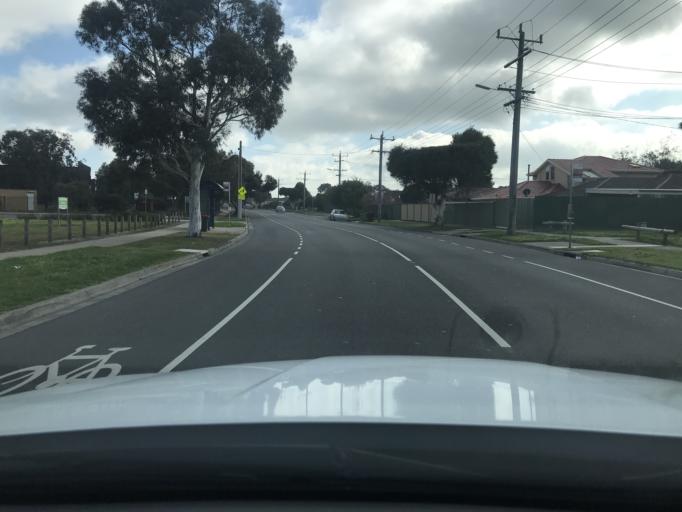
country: AU
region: Victoria
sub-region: Hume
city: Craigieburn
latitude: -37.6102
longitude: 144.9361
